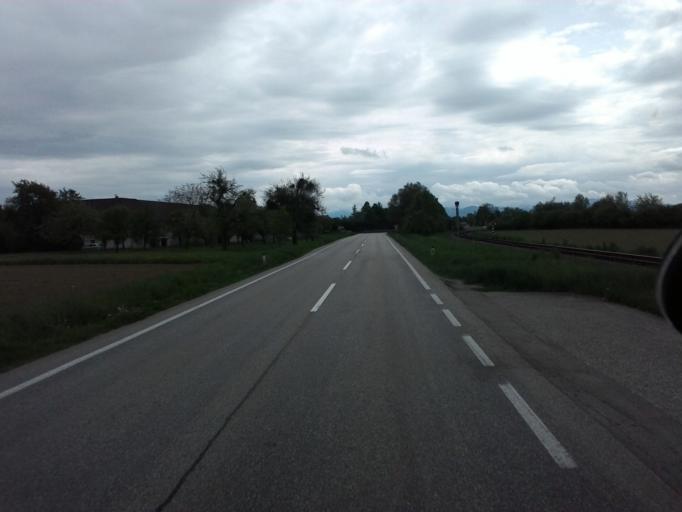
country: AT
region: Upper Austria
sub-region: Wels-Land
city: Sattledt
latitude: 48.0449
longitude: 14.0586
